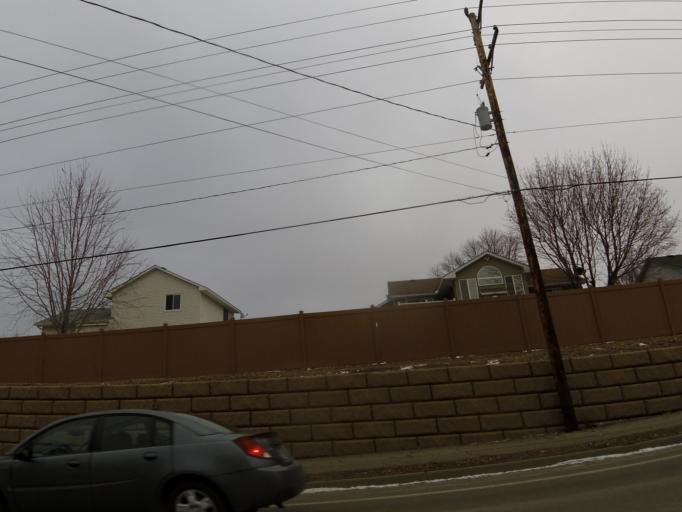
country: US
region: Minnesota
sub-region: Carver County
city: Waconia
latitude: 44.8346
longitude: -93.7885
